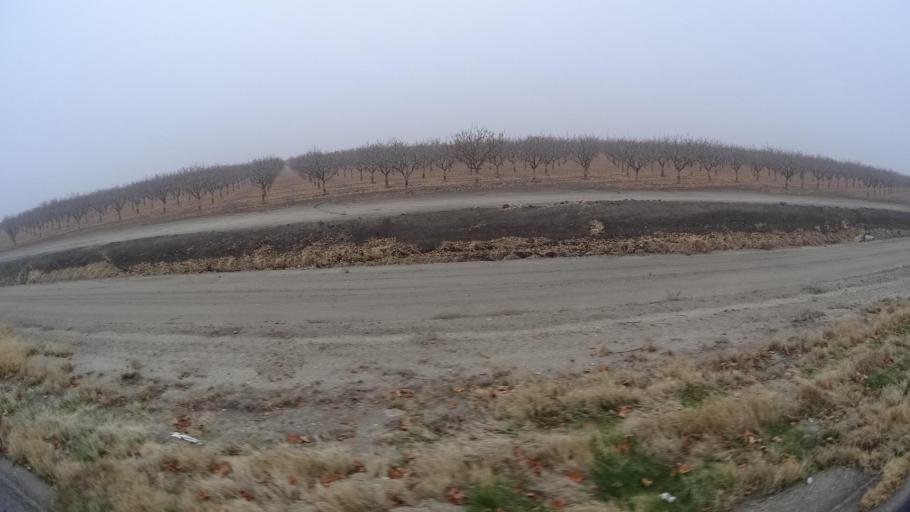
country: US
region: California
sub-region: Kern County
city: Buttonwillow
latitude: 35.4218
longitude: -119.5249
